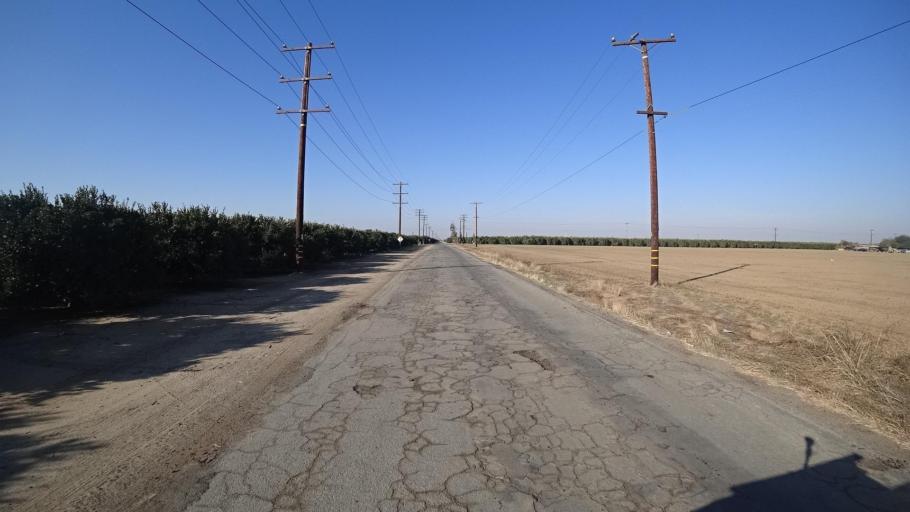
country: US
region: California
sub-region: Tulare County
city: Richgrove
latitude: 35.7327
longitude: -119.1326
